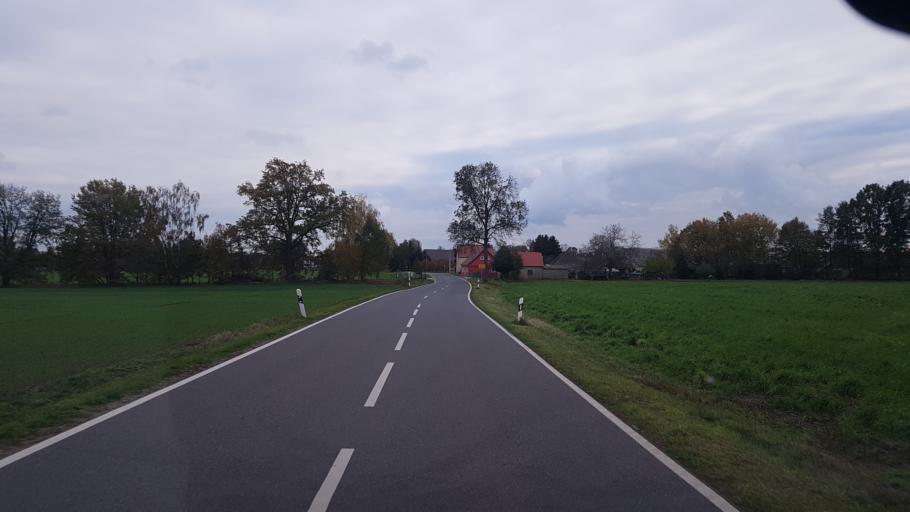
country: DE
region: Brandenburg
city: Finsterwalde
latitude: 51.6079
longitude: 13.6665
